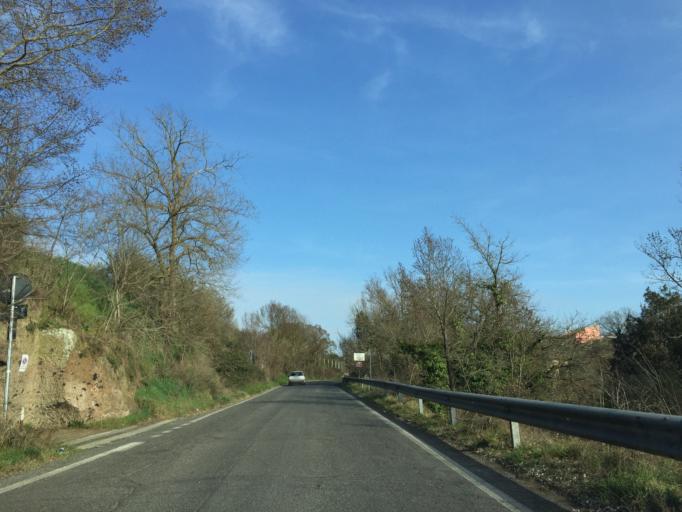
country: IT
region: Latium
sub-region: Provincia di Viterbo
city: Calcata Nuova
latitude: 42.2153
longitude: 12.4240
